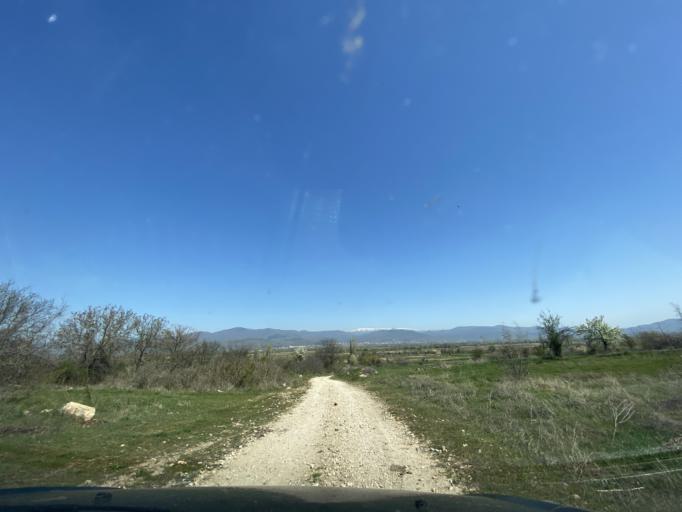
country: MK
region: Zrnovci
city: Zrnovci
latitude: 41.8528
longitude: 22.3895
